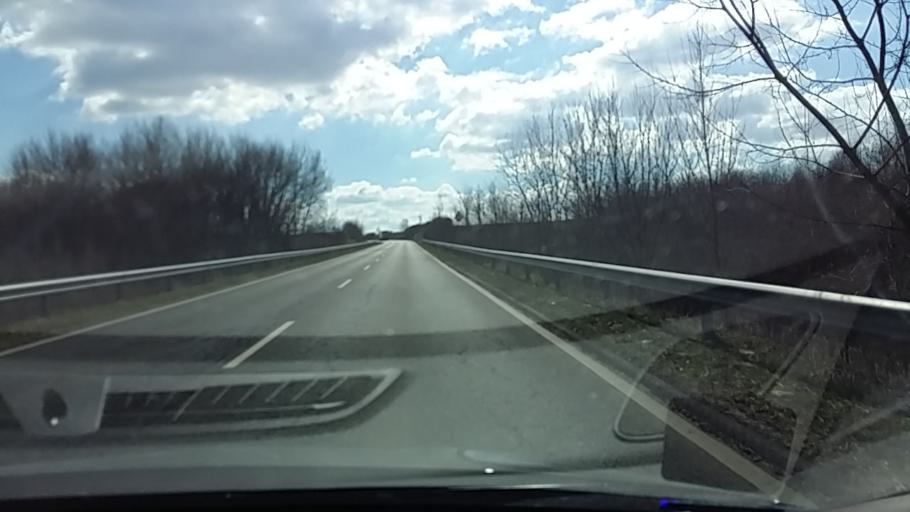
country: HU
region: Baranya
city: Kozarmisleny
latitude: 46.0463
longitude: 18.2728
